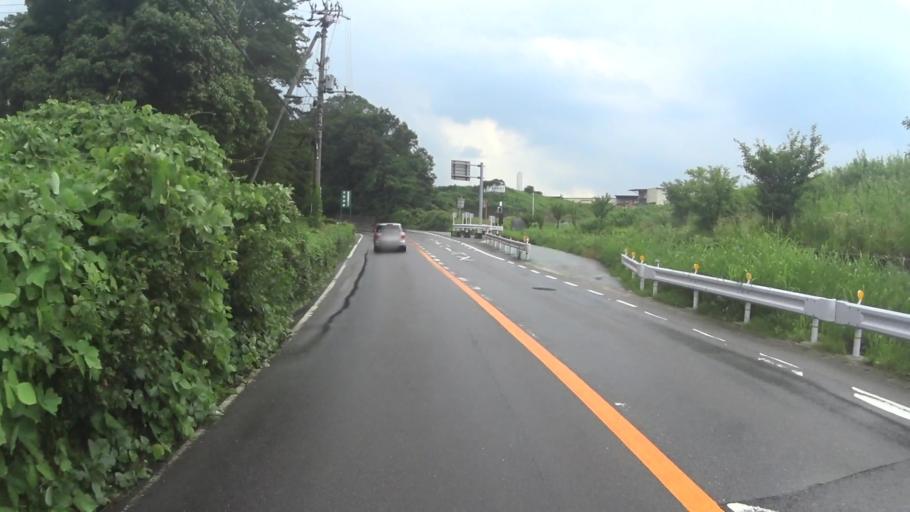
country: JP
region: Kyoto
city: Tanabe
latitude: 34.8075
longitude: 135.7505
